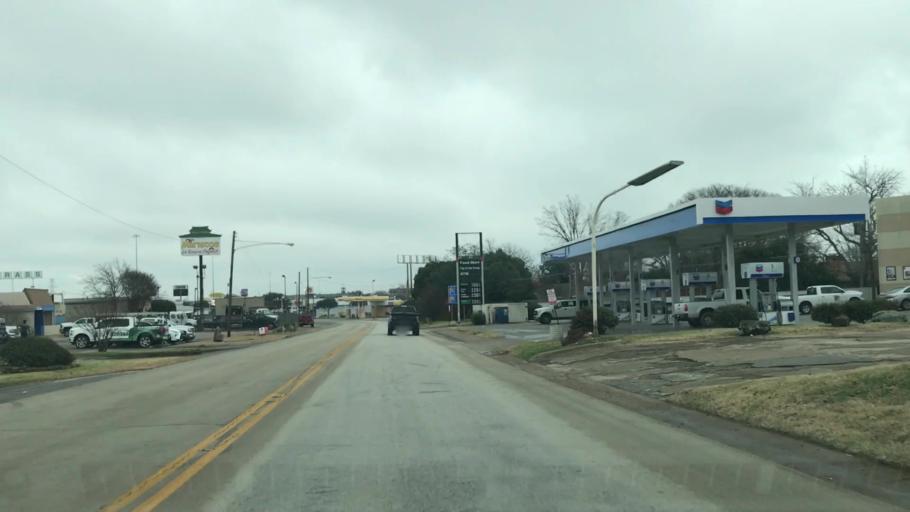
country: US
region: Texas
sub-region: Dallas County
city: Richardson
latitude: 32.8856
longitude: -96.7030
